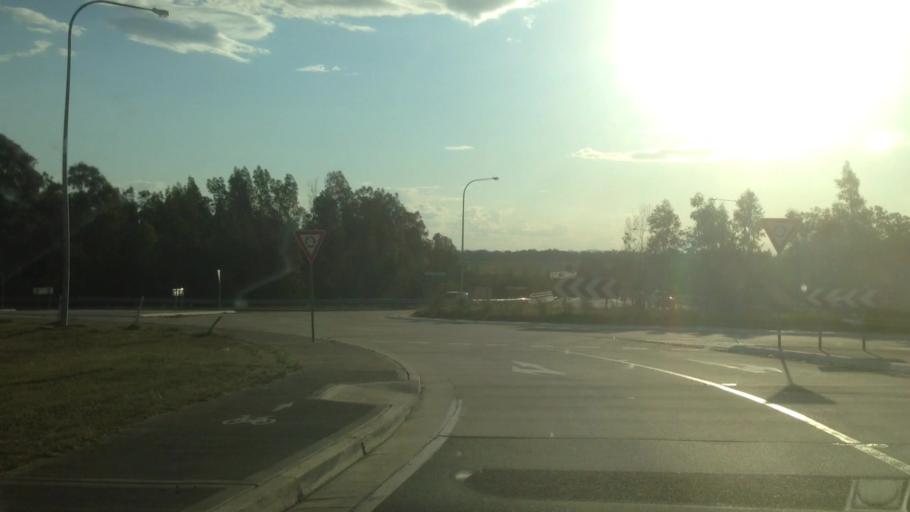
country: AU
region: New South Wales
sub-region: Cessnock
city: Heddon Greta
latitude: -32.8305
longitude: 151.5284
